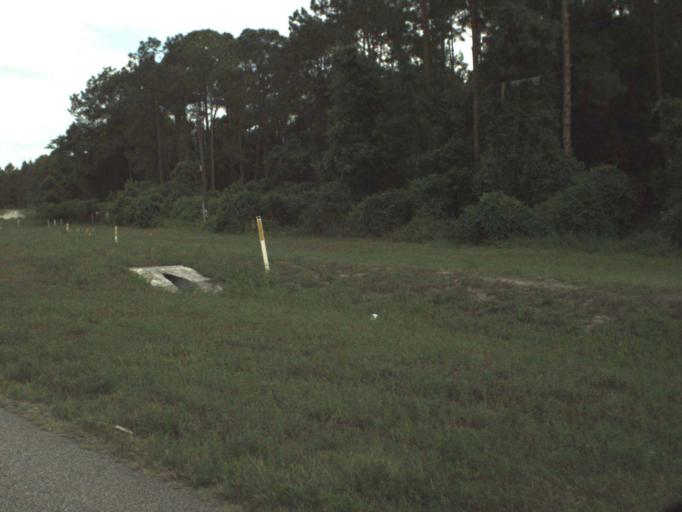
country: US
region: Florida
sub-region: Seminole County
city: Heathrow
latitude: 28.8129
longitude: -81.3877
